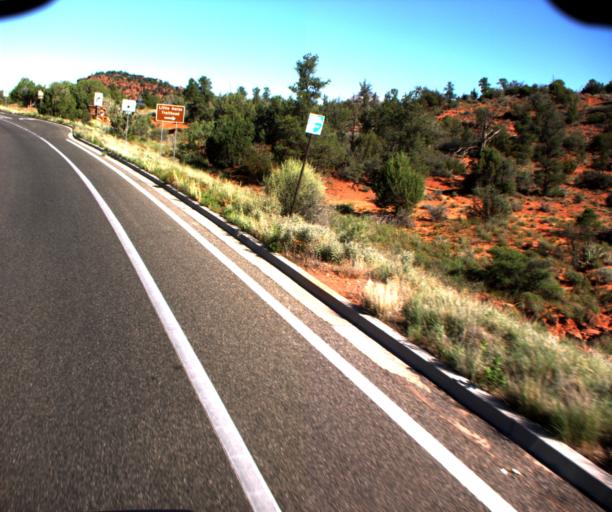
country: US
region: Arizona
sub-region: Yavapai County
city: Village of Oak Creek (Big Park)
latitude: 34.8229
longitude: -111.7745
